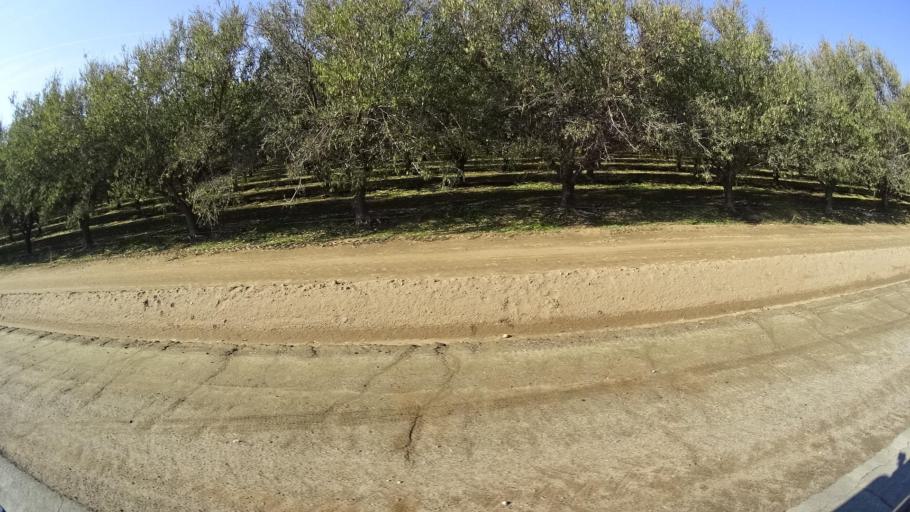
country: US
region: California
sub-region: Kern County
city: Arvin
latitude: 35.2293
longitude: -118.8604
